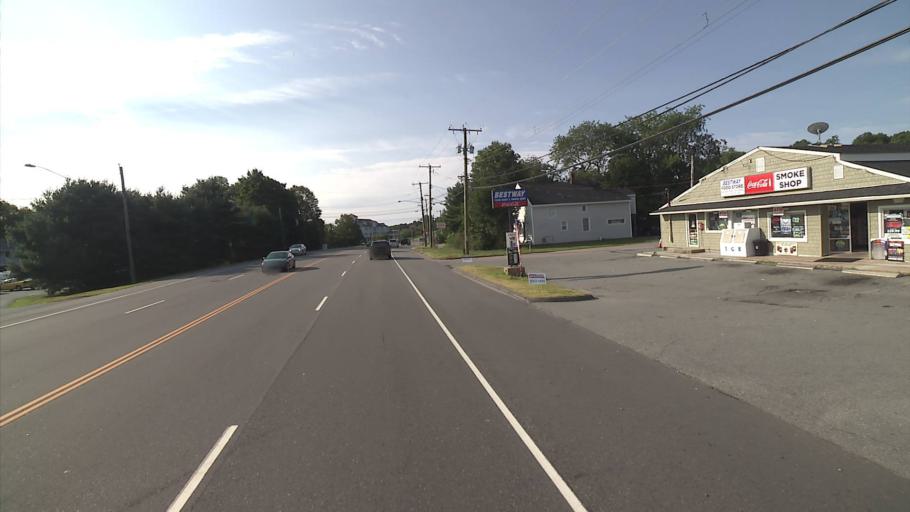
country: US
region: Connecticut
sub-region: New London County
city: Pawcatuck
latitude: 41.4004
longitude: -71.8465
